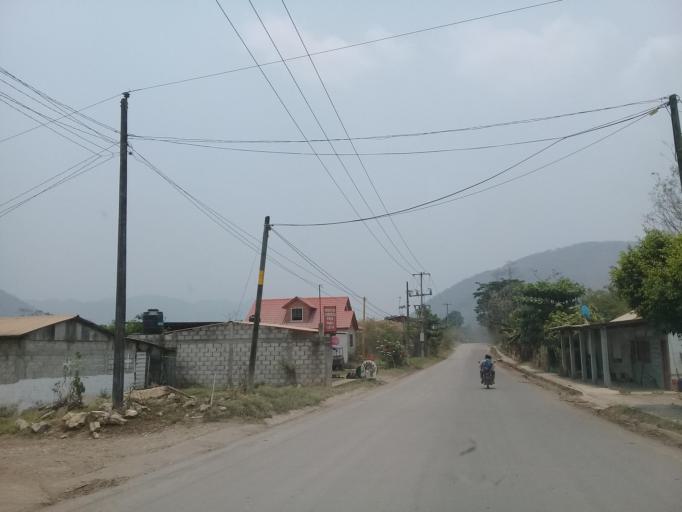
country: MX
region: Veracruz
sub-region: Tezonapa
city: Laguna Chica (Pueblo Nuevo)
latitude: 18.5472
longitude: -96.7306
